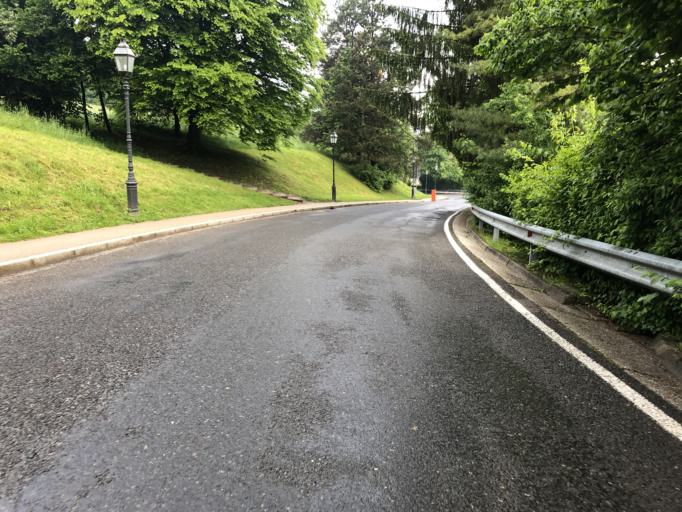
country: SI
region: Ljubljana
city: Ljubljana
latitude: 46.0458
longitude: 14.5151
